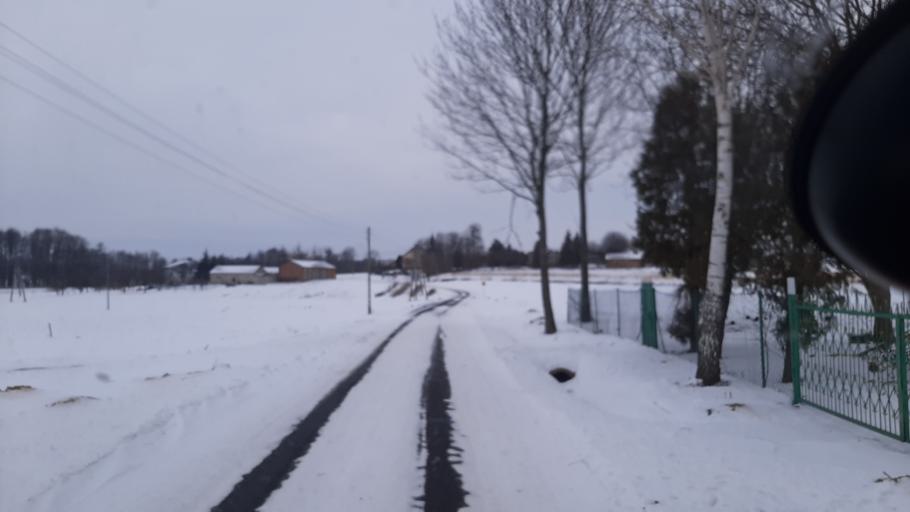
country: PL
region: Lublin Voivodeship
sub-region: Powiat lubelski
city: Garbow
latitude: 51.3403
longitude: 22.2937
